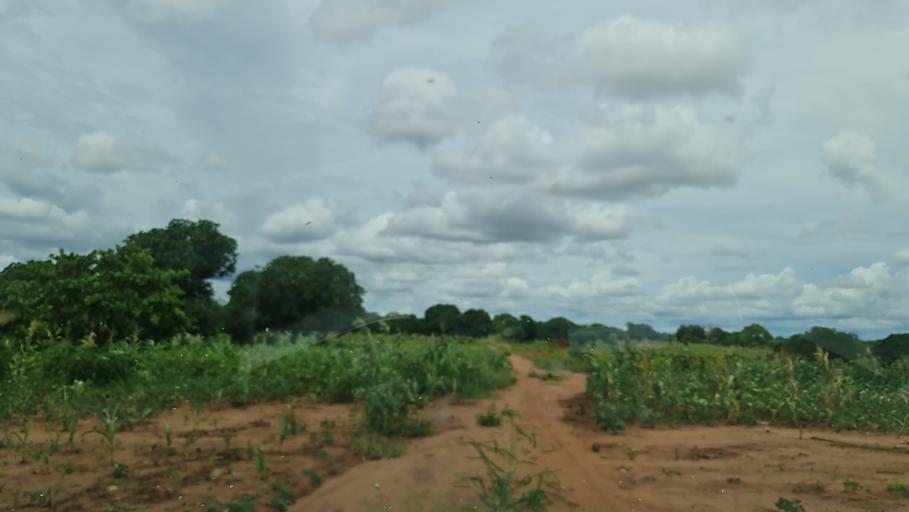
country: MZ
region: Nampula
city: Nacala
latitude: -14.7792
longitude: 39.9885
